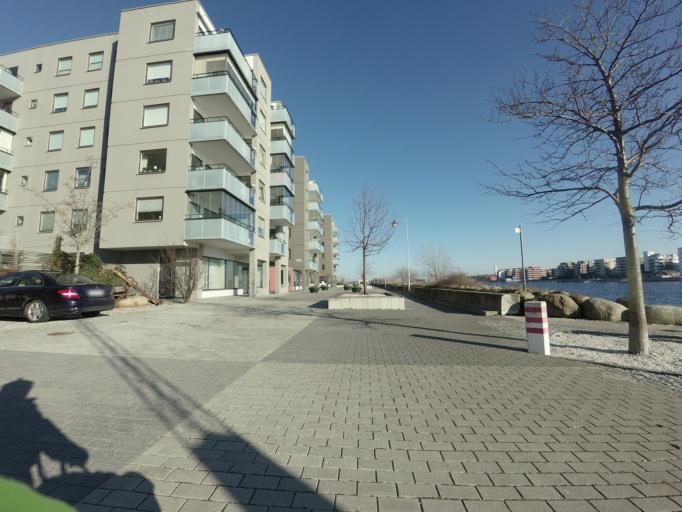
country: SE
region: Skane
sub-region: Malmo
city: Bunkeflostrand
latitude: 55.5907
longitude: 12.9244
